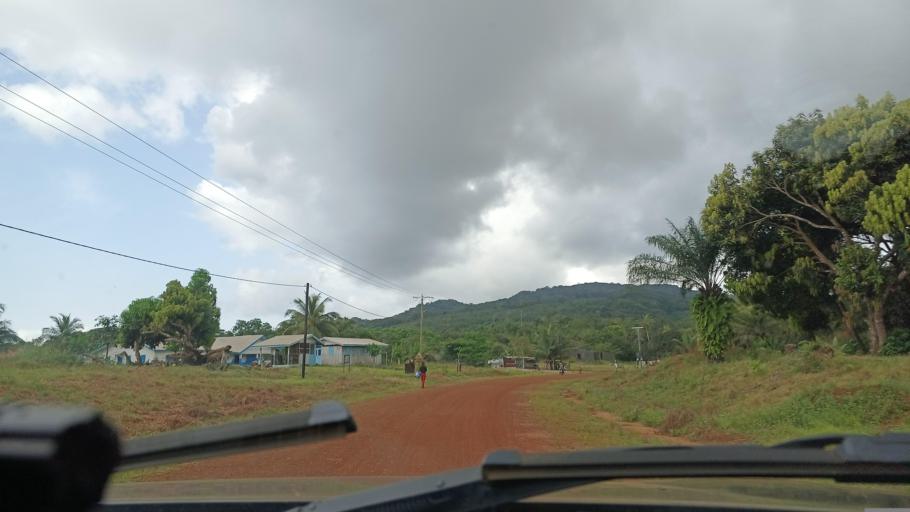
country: LR
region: Grand Cape Mount
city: Robertsport
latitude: 6.7059
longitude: -11.3330
